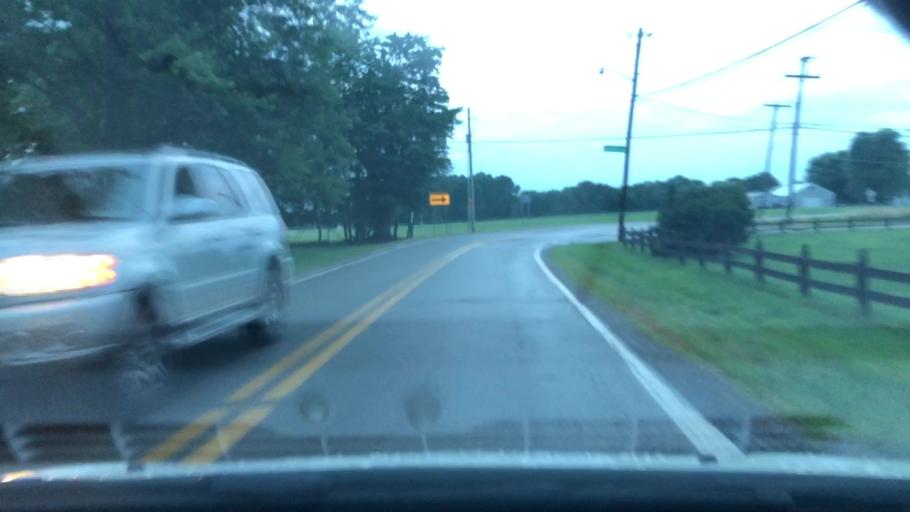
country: US
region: Ohio
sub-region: Franklin County
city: New Albany
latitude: 40.1151
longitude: -82.8587
